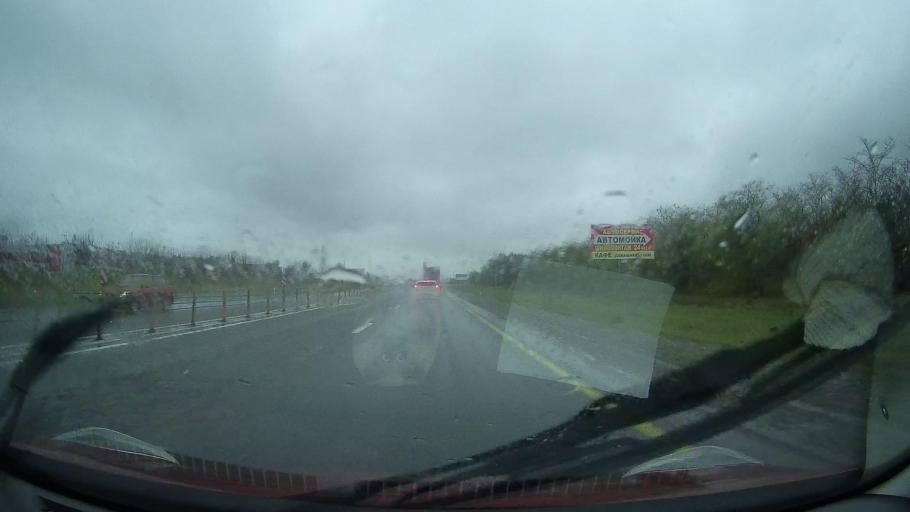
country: RU
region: Stavropol'skiy
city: Nevinnomyssk
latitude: 44.6414
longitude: 41.9643
